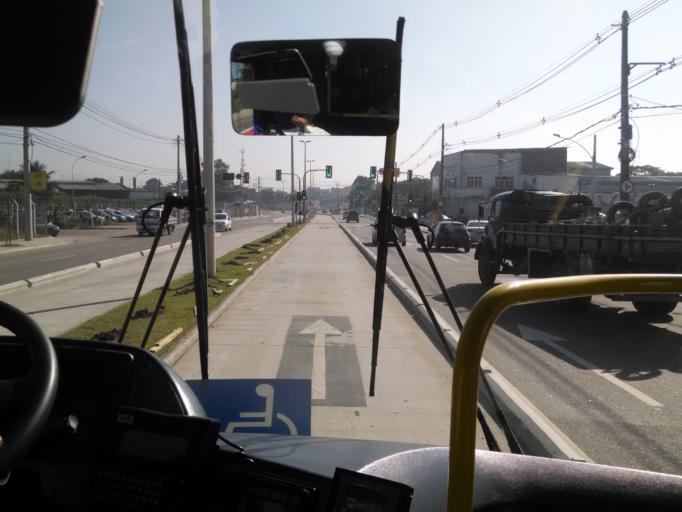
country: BR
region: Rio de Janeiro
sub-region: Nilopolis
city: Nilopolis
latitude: -22.9639
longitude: -43.3904
